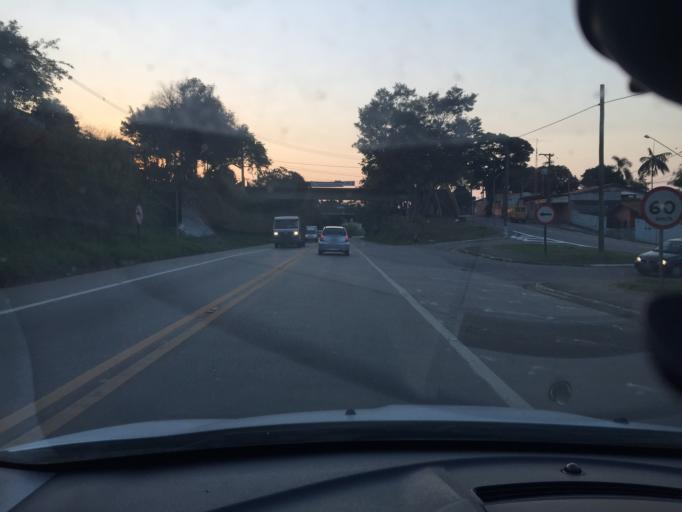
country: BR
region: Sao Paulo
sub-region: Varzea Paulista
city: Varzea Paulista
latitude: -23.2443
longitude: -46.8509
